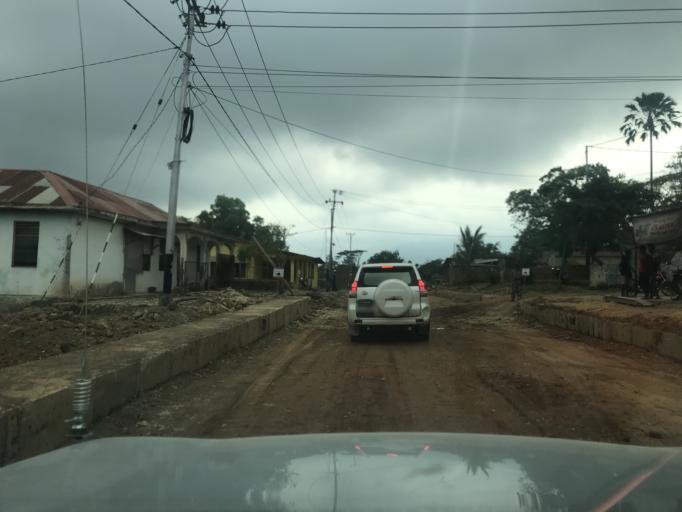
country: TL
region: Ainaro
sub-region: Ainaro
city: Ainaro
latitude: -8.9965
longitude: 125.5057
